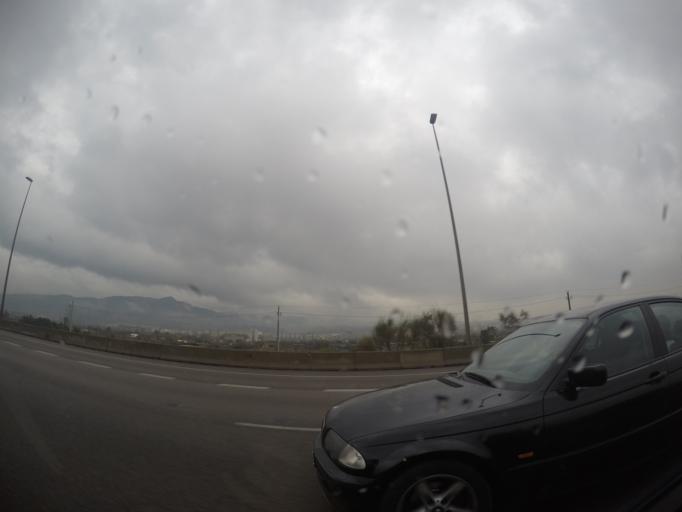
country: ES
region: Catalonia
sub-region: Provincia de Barcelona
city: Sant Feliu de Llobregat
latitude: 41.3853
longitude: 2.0282
